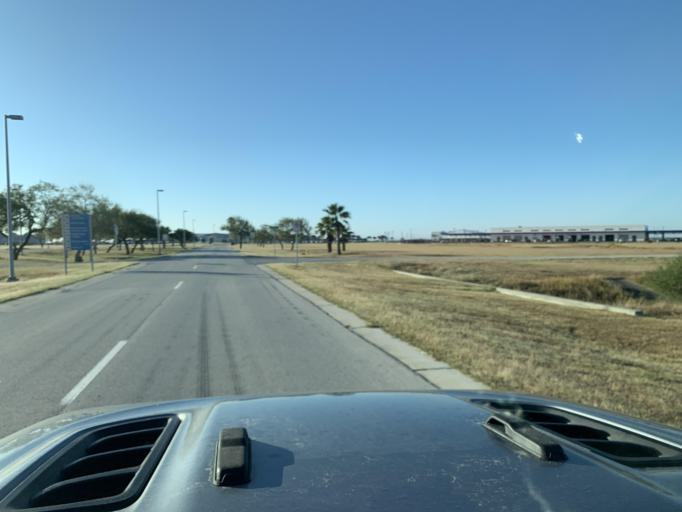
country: US
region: Texas
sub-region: Nueces County
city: Corpus Christi
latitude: 27.7807
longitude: -97.5024
